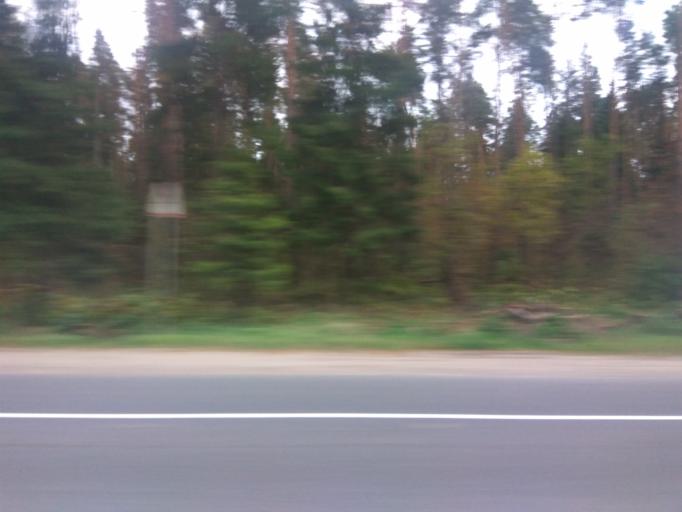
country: RU
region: Moskovskaya
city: Krasnoarmeysk
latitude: 56.0334
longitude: 38.1908
